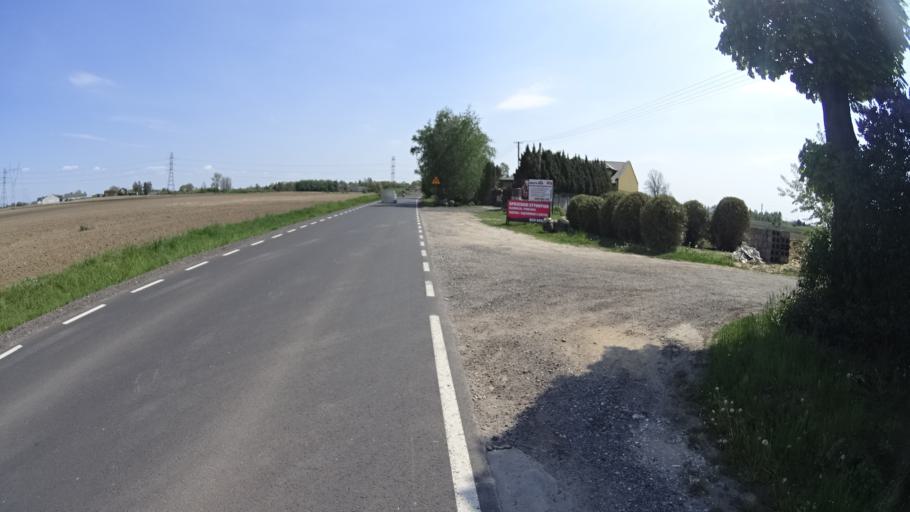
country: PL
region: Masovian Voivodeship
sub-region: Powiat warszawski zachodni
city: Ozarow Mazowiecki
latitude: 52.2368
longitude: 20.7561
